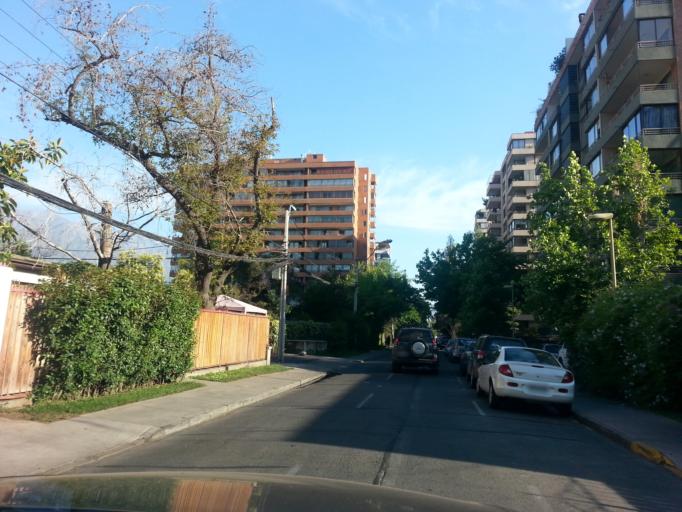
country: CL
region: Santiago Metropolitan
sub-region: Provincia de Santiago
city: Villa Presidente Frei, Nunoa, Santiago, Chile
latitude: -33.4175
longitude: -70.5671
